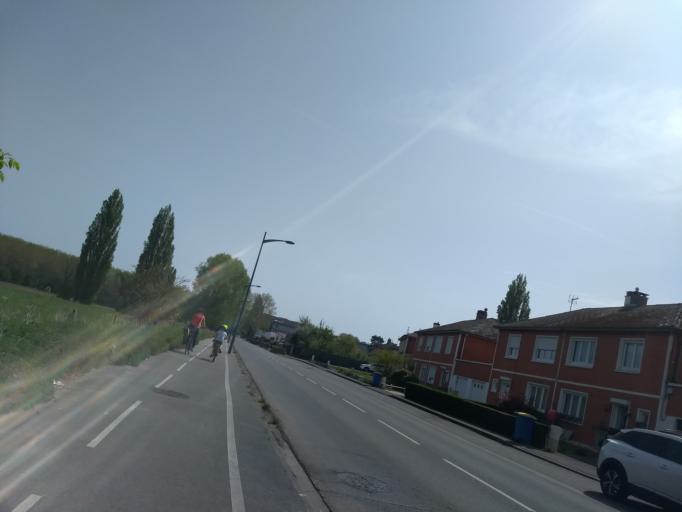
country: FR
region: Nord-Pas-de-Calais
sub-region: Departement du Pas-de-Calais
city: Anzin-Saint-Aubin
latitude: 50.3044
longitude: 2.7484
